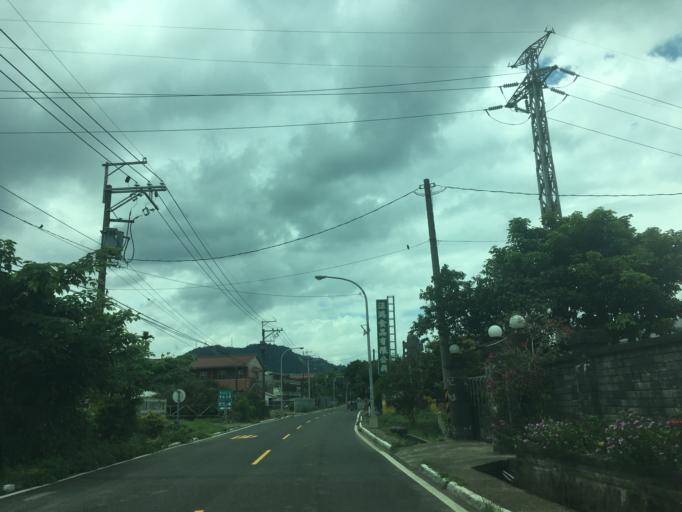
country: TW
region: Taiwan
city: Daxi
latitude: 24.8536
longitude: 121.2904
